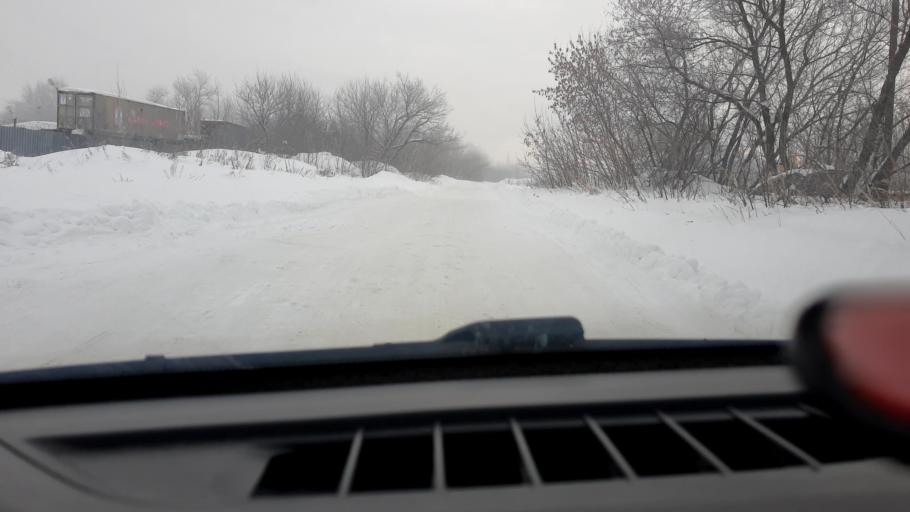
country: RU
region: Nizjnij Novgorod
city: Babino
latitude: 56.2622
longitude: 43.6042
